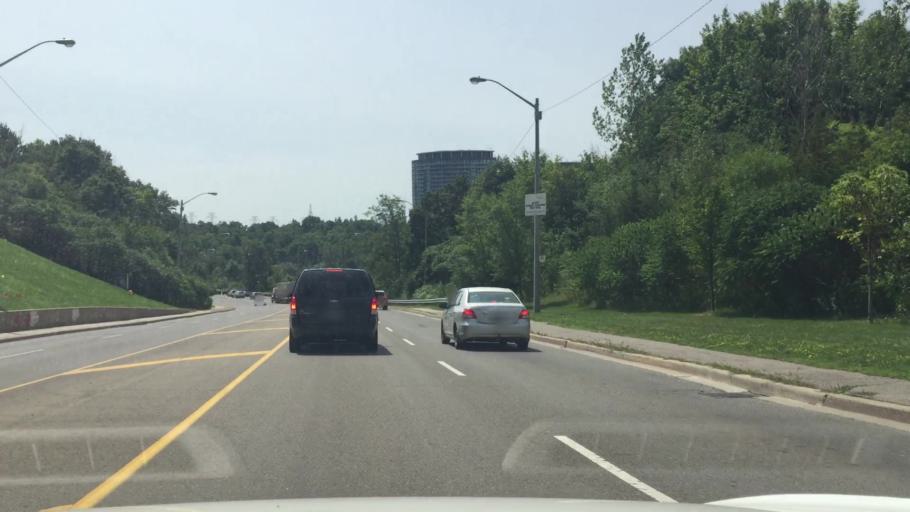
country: CA
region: Ontario
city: Willowdale
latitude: 43.7202
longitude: -79.3500
